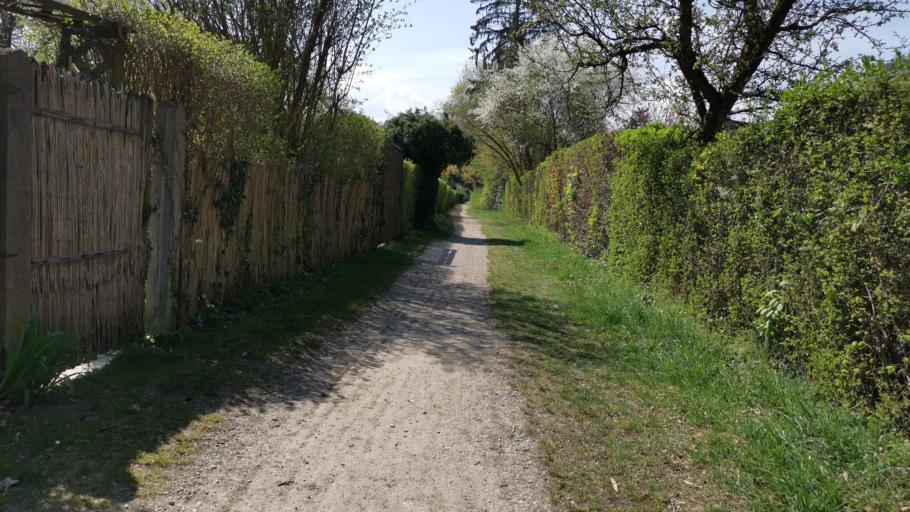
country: DE
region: Bavaria
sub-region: Upper Bavaria
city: Pullach im Isartal
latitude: 48.0855
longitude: 11.5288
